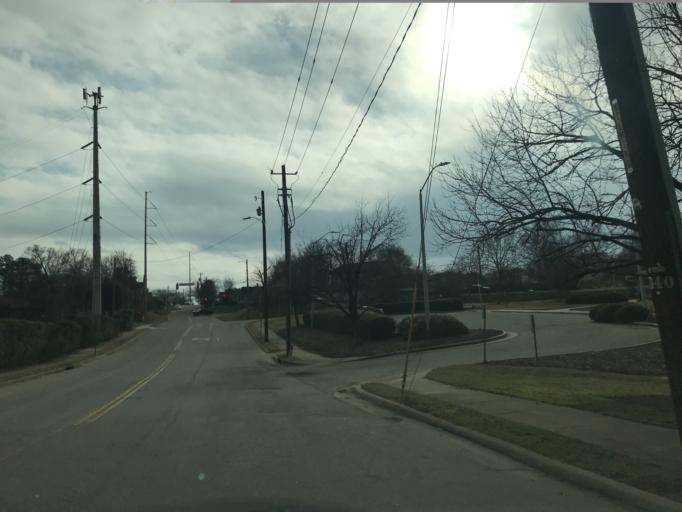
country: US
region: North Carolina
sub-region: Wake County
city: Raleigh
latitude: 35.7698
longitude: -78.6328
